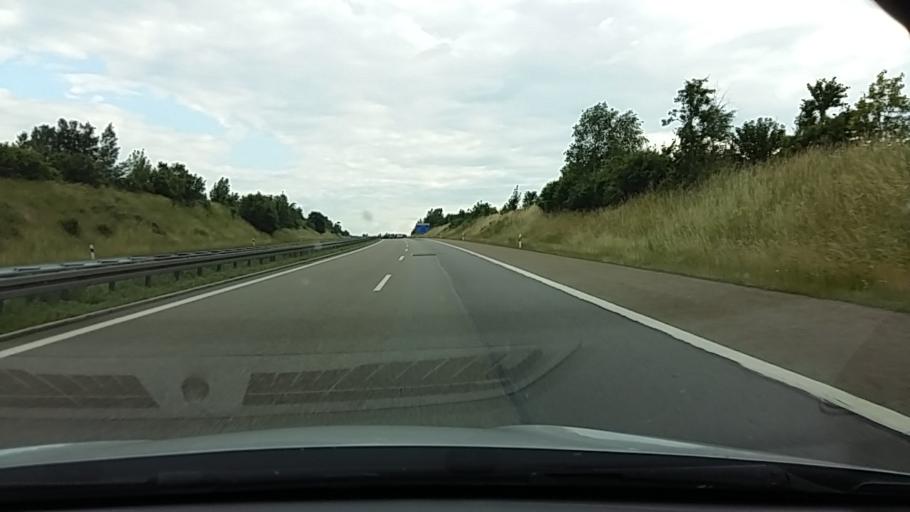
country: DE
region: Bavaria
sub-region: Upper Palatinate
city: Vohenstrauss
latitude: 49.6063
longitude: 12.3261
